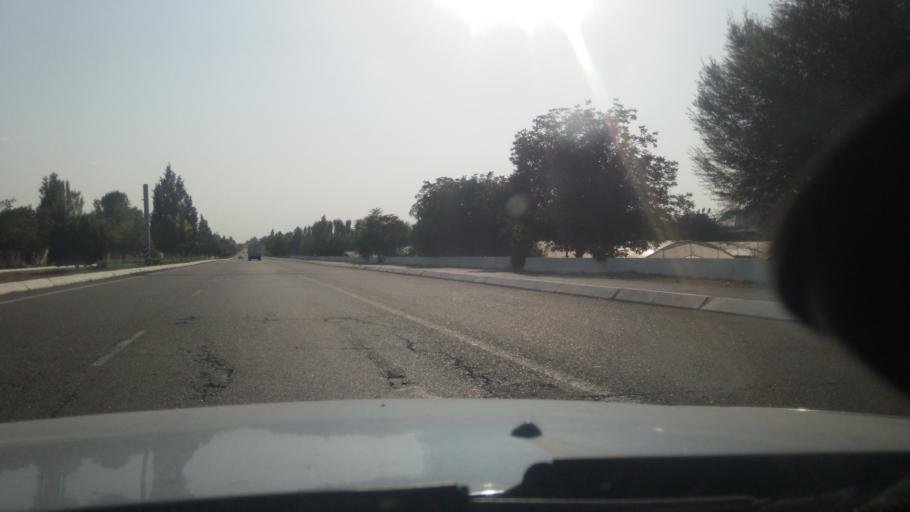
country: UZ
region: Toshkent
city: Zafar
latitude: 41.0104
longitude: 68.8377
